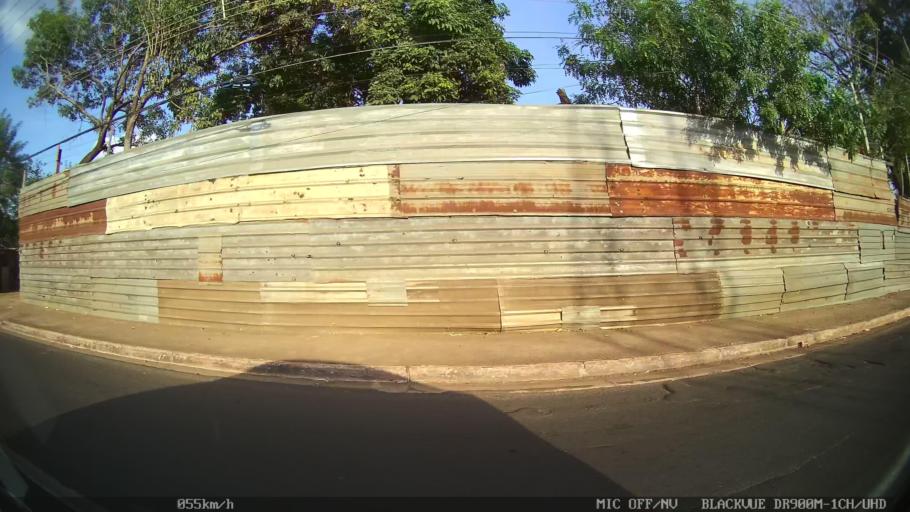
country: BR
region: Sao Paulo
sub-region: Ribeirao Preto
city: Ribeirao Preto
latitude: -21.1465
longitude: -47.8044
